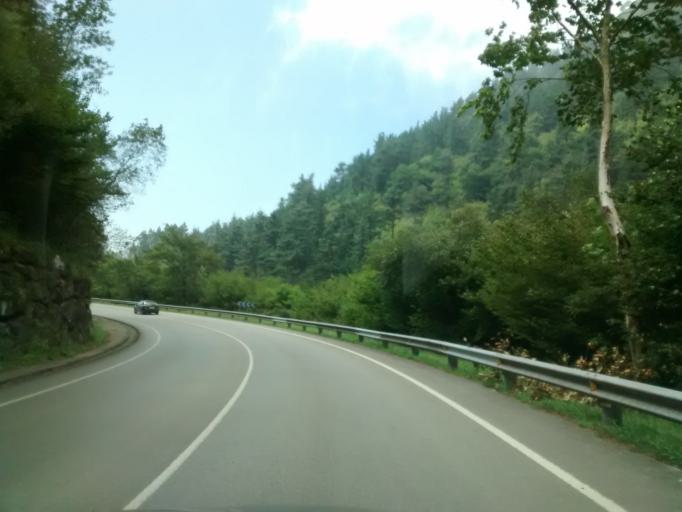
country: ES
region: Cantabria
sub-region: Provincia de Cantabria
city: Ruente
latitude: 43.2768
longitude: -4.2452
